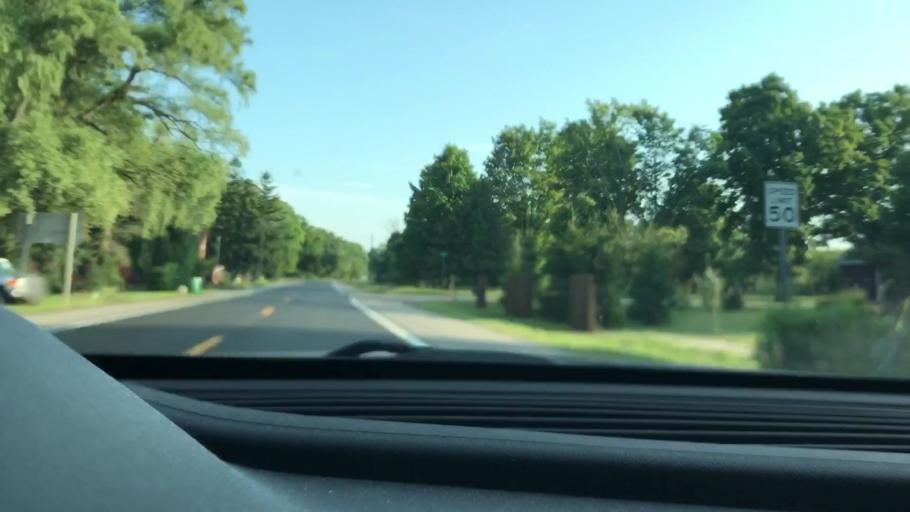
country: US
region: Michigan
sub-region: Antrim County
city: Bellaire
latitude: 45.0756
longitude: -85.3588
